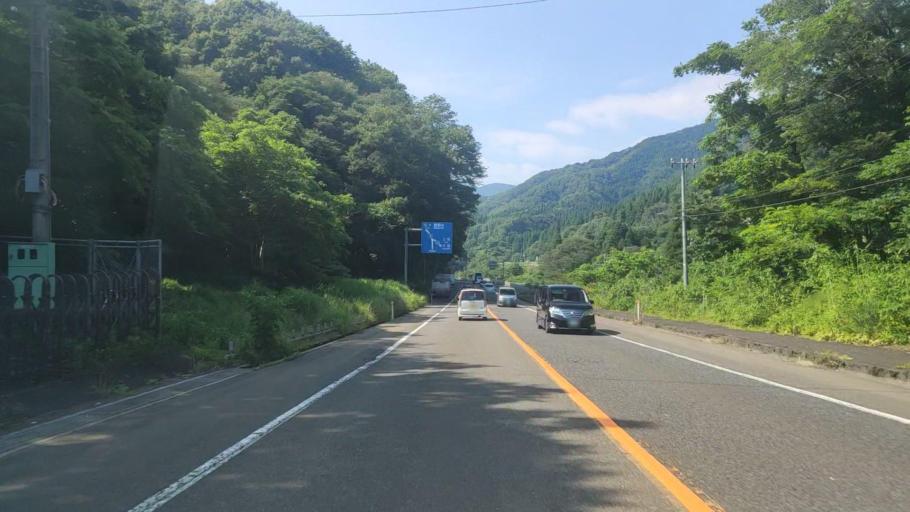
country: JP
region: Fukui
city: Tsuruga
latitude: 35.6039
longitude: 136.1222
